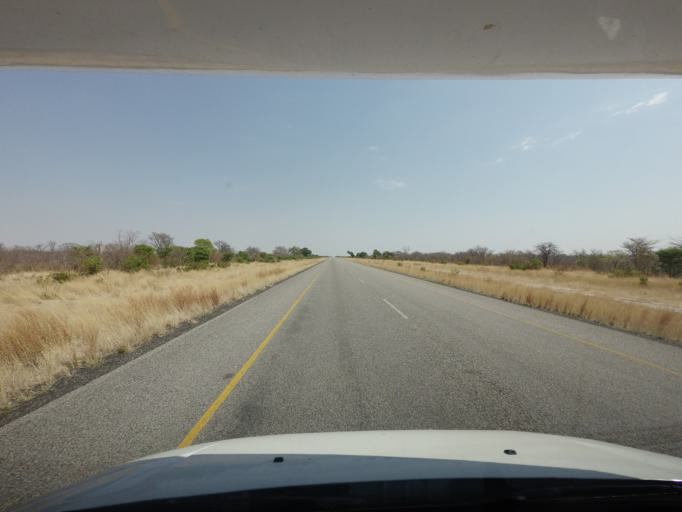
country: BW
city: Pandamatenga
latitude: -18.9717
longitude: 25.6666
